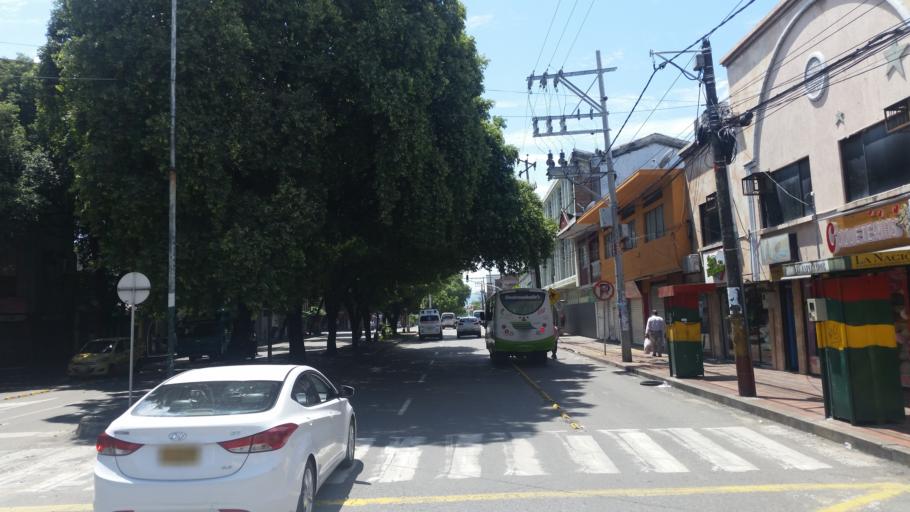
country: CO
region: Huila
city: Neiva
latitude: 2.9286
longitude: -75.2871
